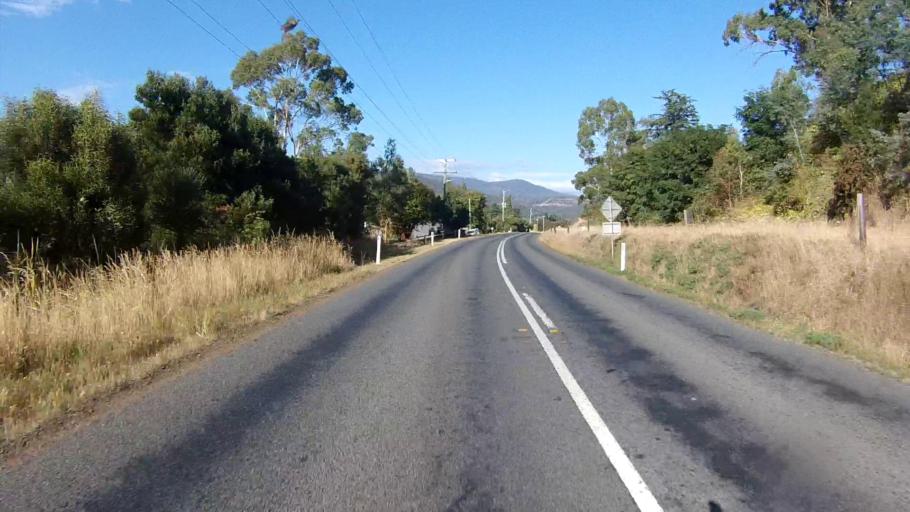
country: AU
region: Tasmania
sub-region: Derwent Valley
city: New Norfolk
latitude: -42.7731
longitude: 147.0654
